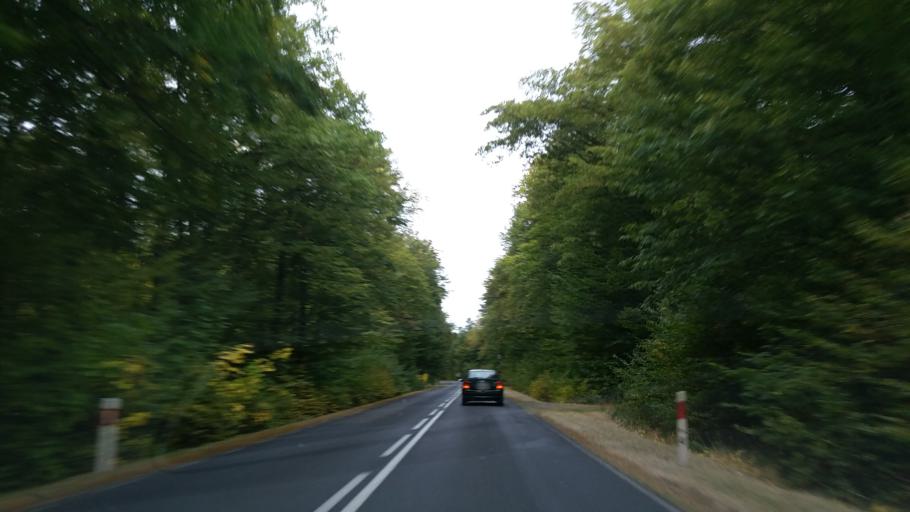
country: PL
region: Lubusz
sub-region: Powiat gorzowski
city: Klodawa
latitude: 52.8575
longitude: 15.2006
